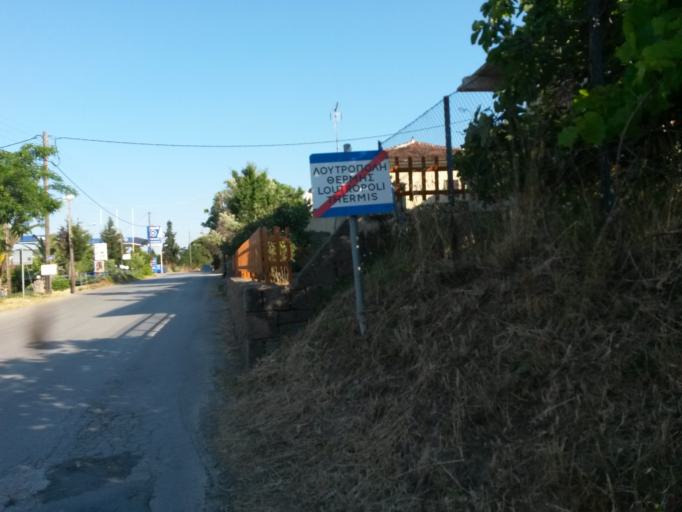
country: GR
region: North Aegean
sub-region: Nomos Lesvou
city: Pamfylla
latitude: 39.1801
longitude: 26.4987
